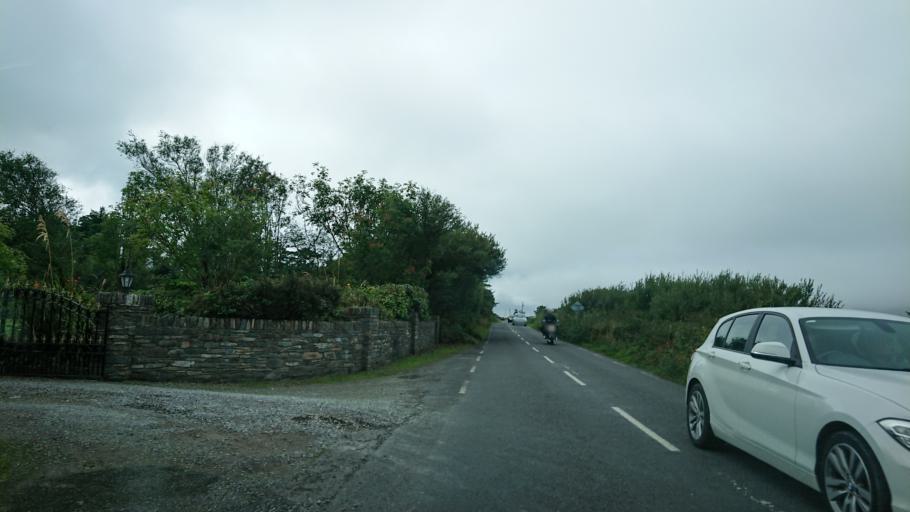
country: IE
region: Munster
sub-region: Ciarrai
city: Cahersiveen
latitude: 51.9326
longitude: -10.2515
